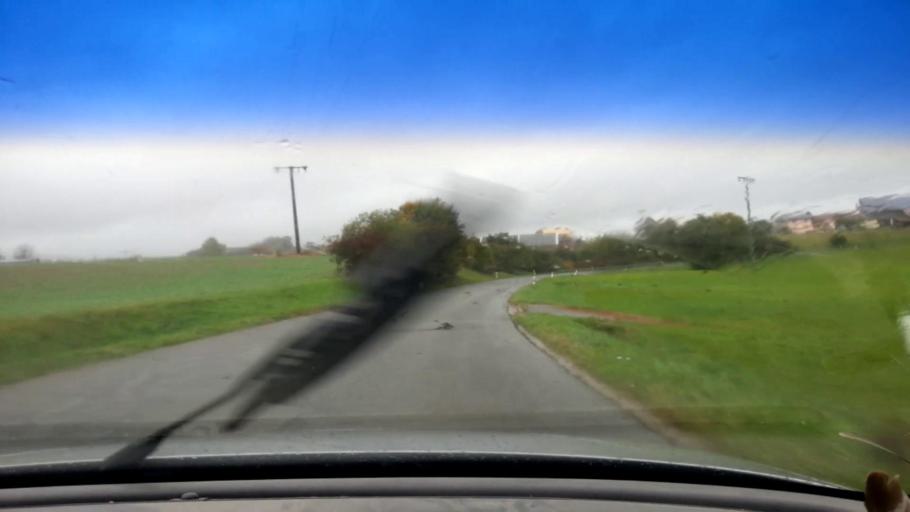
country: DE
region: Bavaria
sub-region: Upper Franconia
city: Stadelhofen
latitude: 50.0233
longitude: 11.1815
